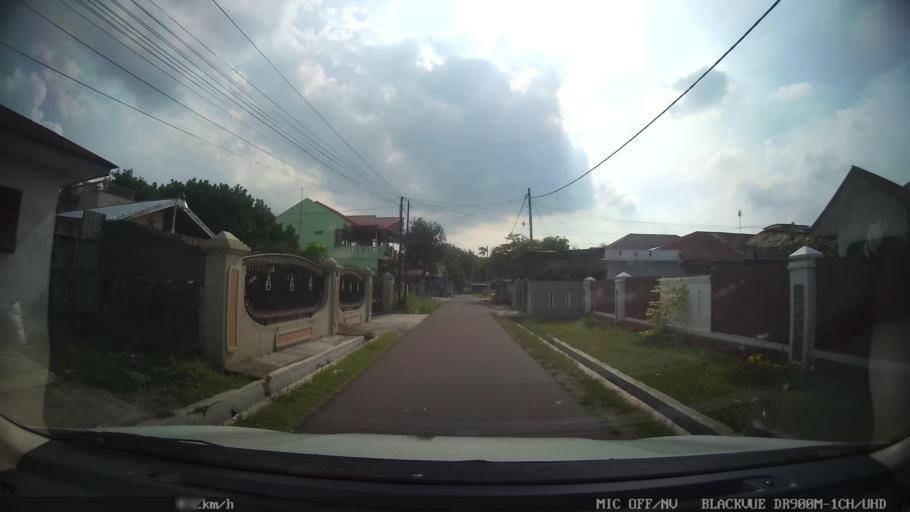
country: ID
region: North Sumatra
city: Binjai
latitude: 3.6037
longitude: 98.4938
